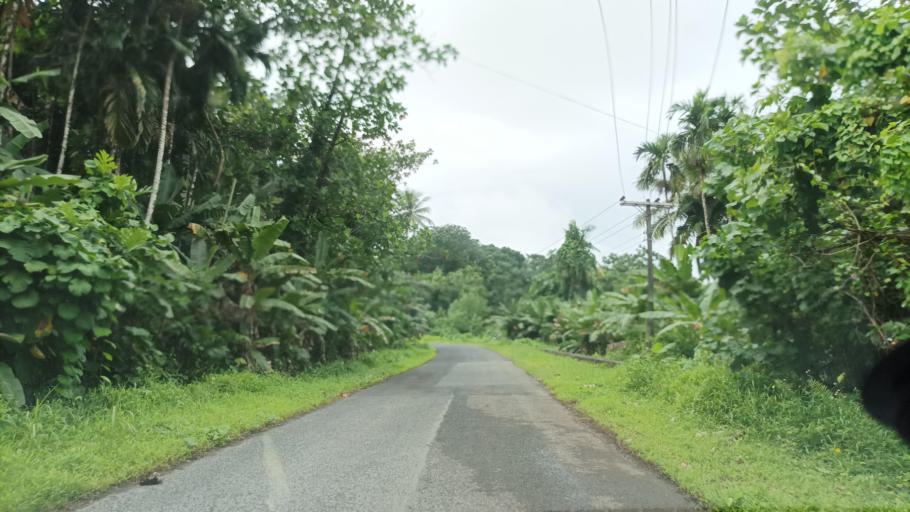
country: FM
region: Pohnpei
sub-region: Madolenihm Municipality
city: Madolenihm Municipality Government
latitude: 6.9021
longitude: 158.3184
